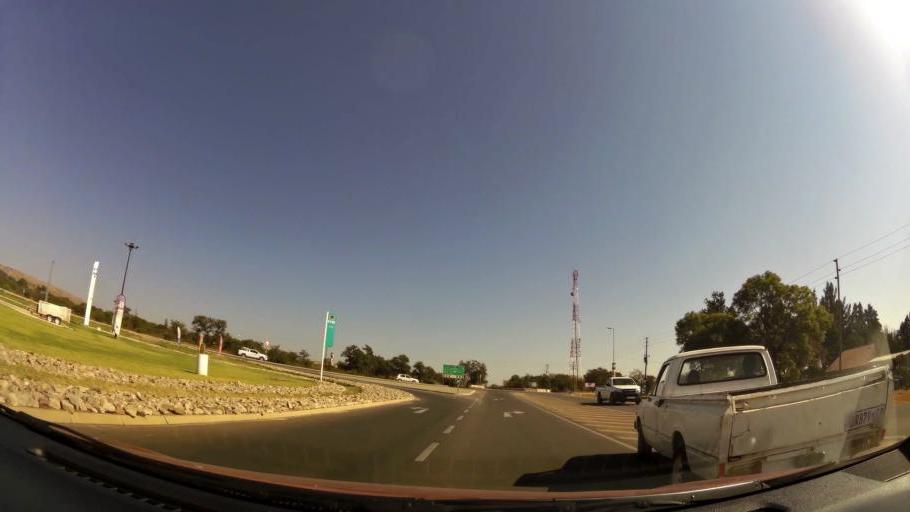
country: ZA
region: North-West
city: Ga-Rankuwa
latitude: -25.6609
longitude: 28.0463
